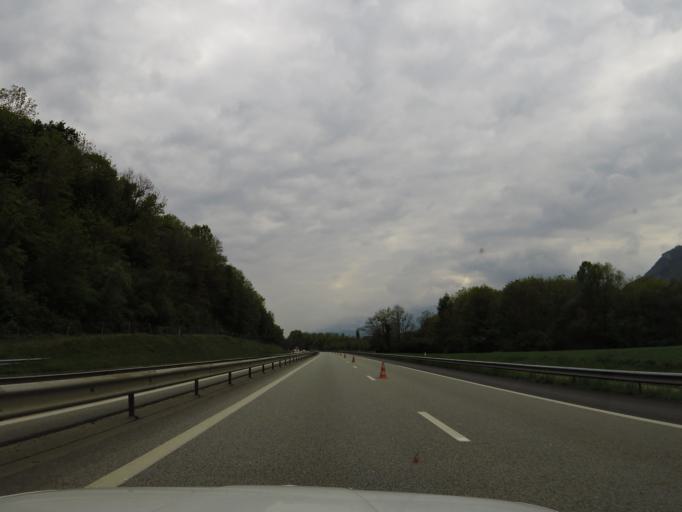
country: FR
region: Rhone-Alpes
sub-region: Departement de la Savoie
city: Cruet
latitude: 45.5261
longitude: 6.1166
